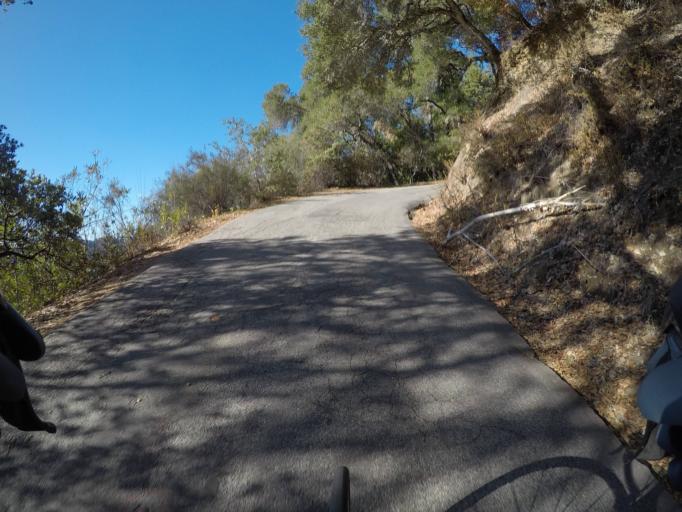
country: US
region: California
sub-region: Santa Clara County
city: Lexington Hills
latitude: 37.1096
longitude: -121.9924
